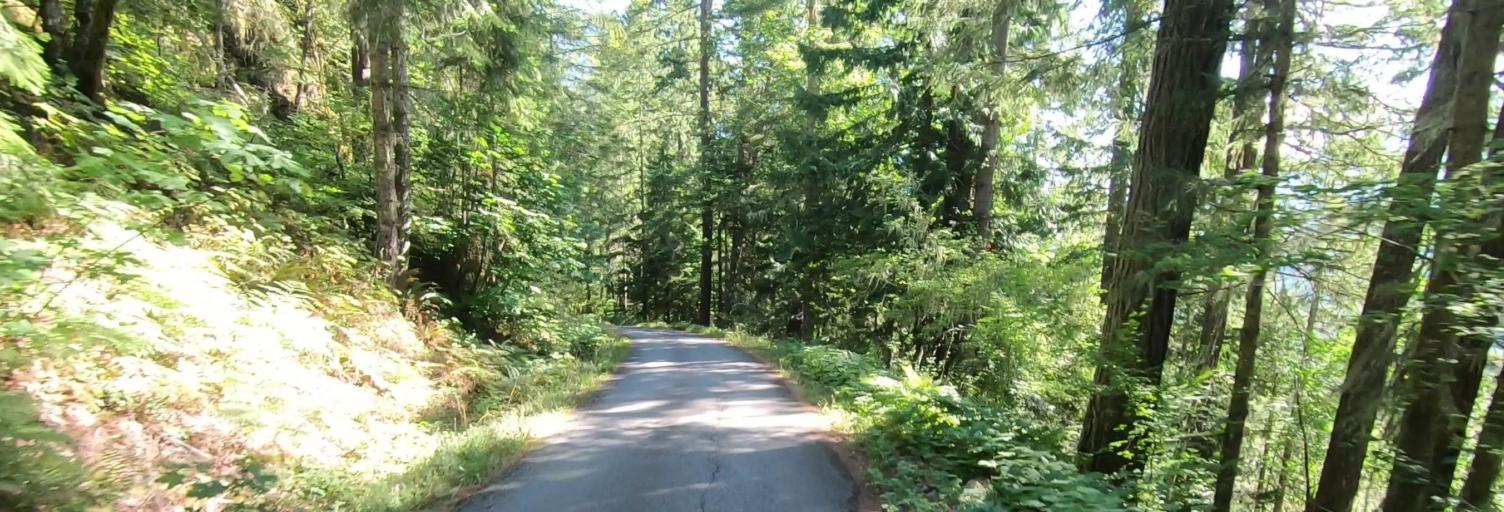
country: US
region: Washington
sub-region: Whatcom County
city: Peaceful Valley
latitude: 48.9051
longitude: -121.9309
